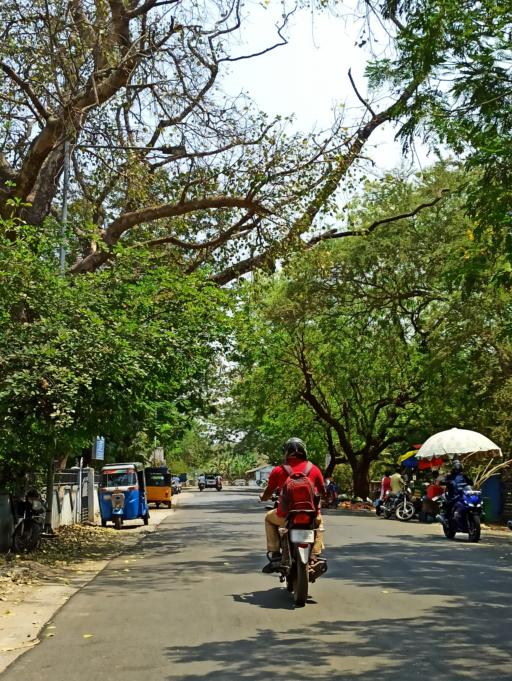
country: IN
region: Tamil Nadu
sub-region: Thiruvallur
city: Chinnasekkadu
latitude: 13.1628
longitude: 80.2450
